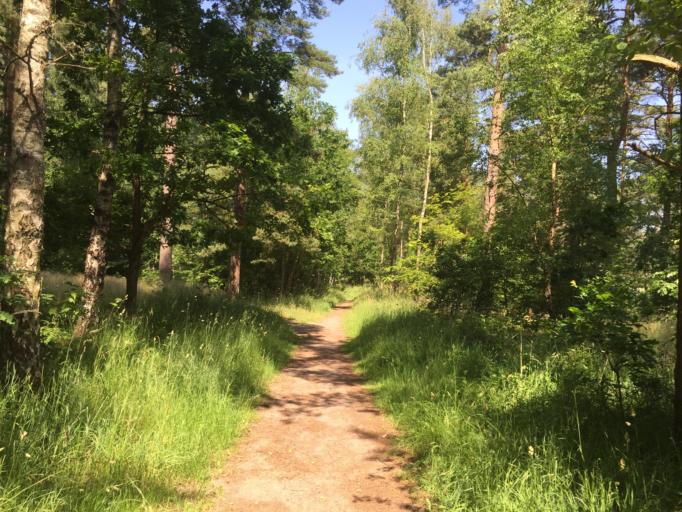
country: SE
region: Skane
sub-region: Lunds Kommun
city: Veberod
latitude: 55.6228
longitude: 13.5075
